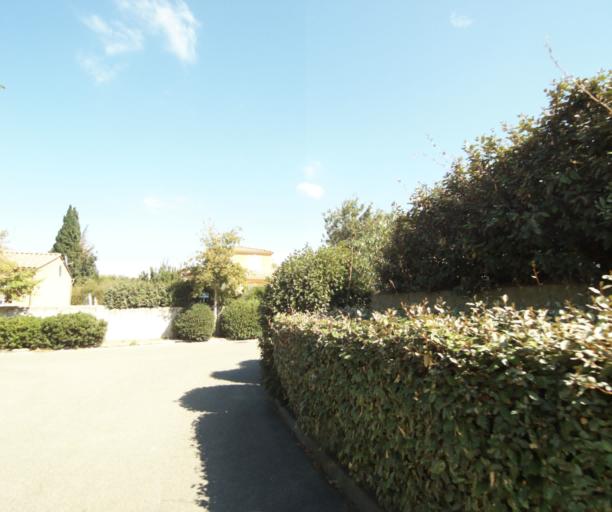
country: FR
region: Languedoc-Roussillon
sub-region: Departement du Gard
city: Bouillargues
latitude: 43.8032
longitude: 4.4349
